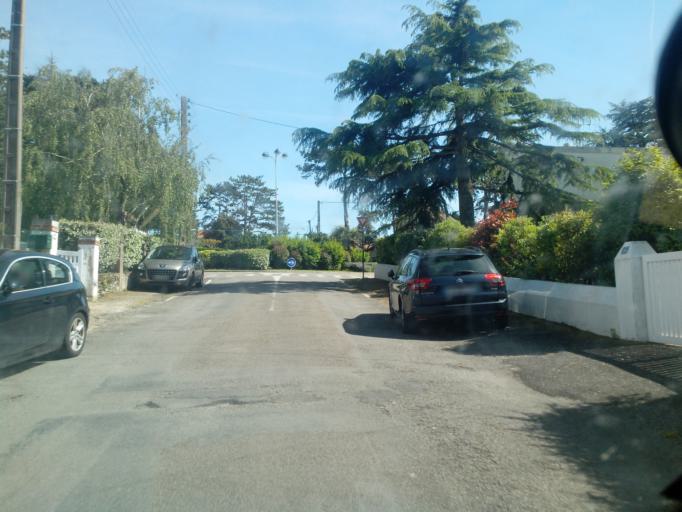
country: FR
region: Pays de la Loire
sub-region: Departement de la Loire-Atlantique
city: Pornic
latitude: 47.1110
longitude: -2.1028
